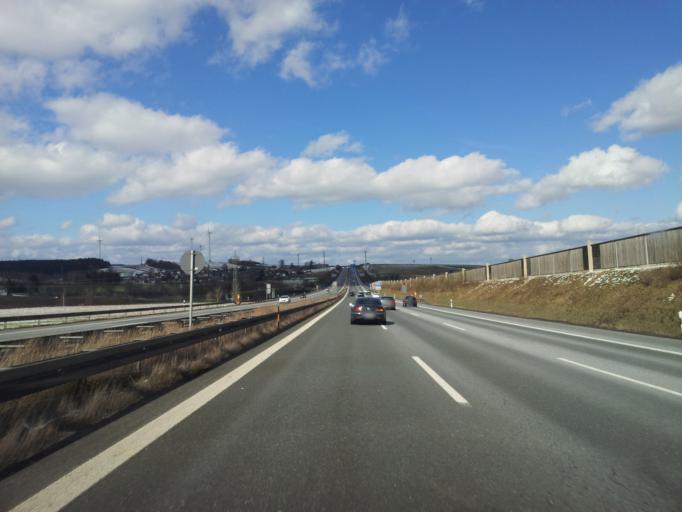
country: DE
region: Bavaria
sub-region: Upper Franconia
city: Munchberg
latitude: 50.1876
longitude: 11.7626
